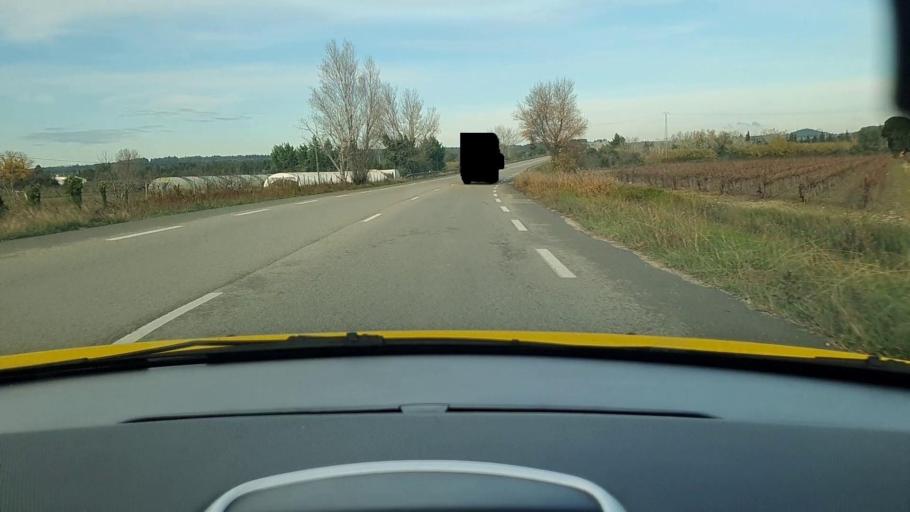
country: FR
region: Languedoc-Roussillon
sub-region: Departement du Gard
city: Beaucaire
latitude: 43.7940
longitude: 4.6118
